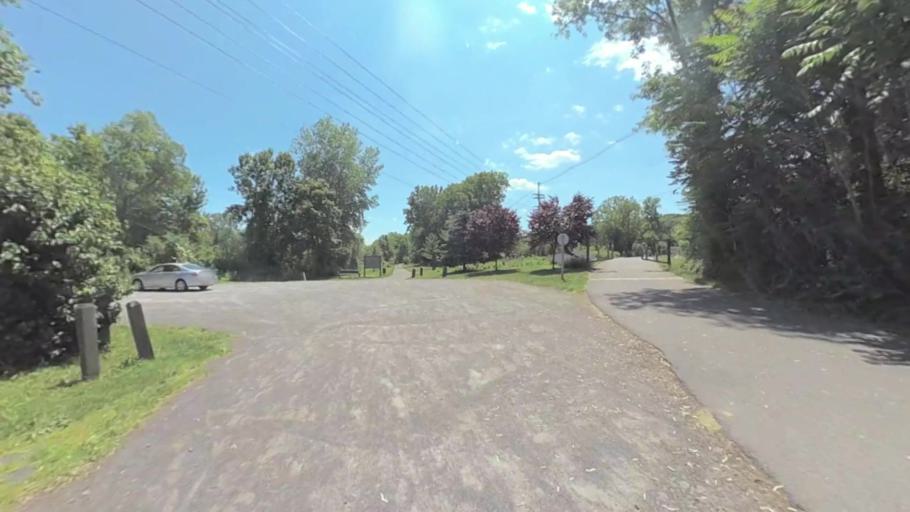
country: US
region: New York
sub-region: Monroe County
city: Fairport
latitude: 43.1002
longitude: -77.4370
